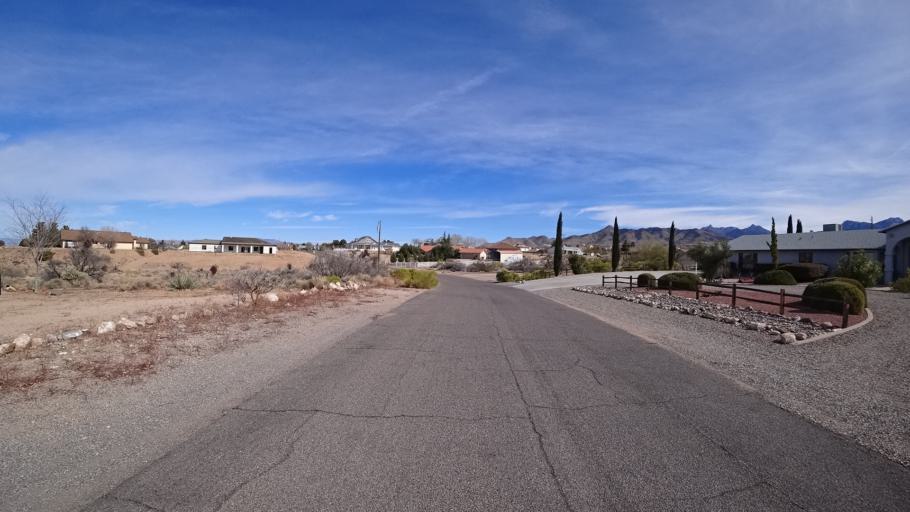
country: US
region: Arizona
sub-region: Mohave County
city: Kingman
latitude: 35.1912
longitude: -113.9913
